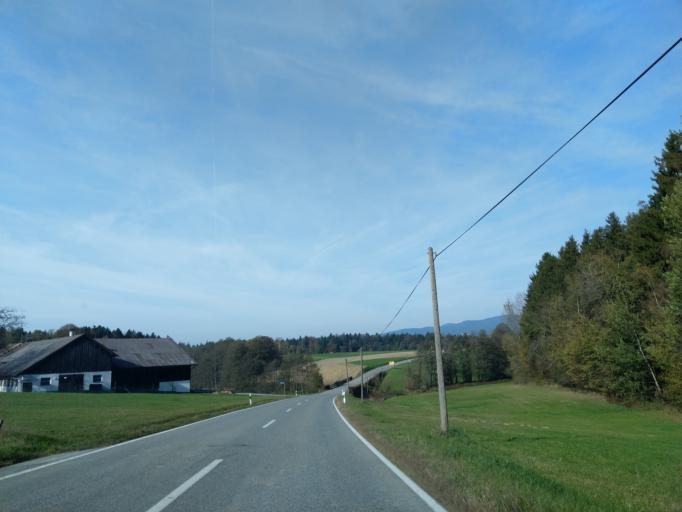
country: DE
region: Bavaria
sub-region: Lower Bavaria
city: Grattersdorf
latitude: 48.8107
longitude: 13.1286
